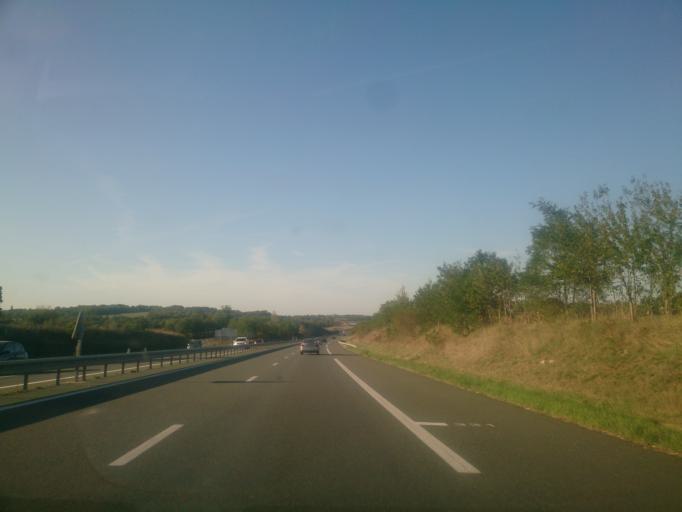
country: FR
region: Midi-Pyrenees
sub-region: Departement du Lot
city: Le Vigan
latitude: 44.6865
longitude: 1.5715
